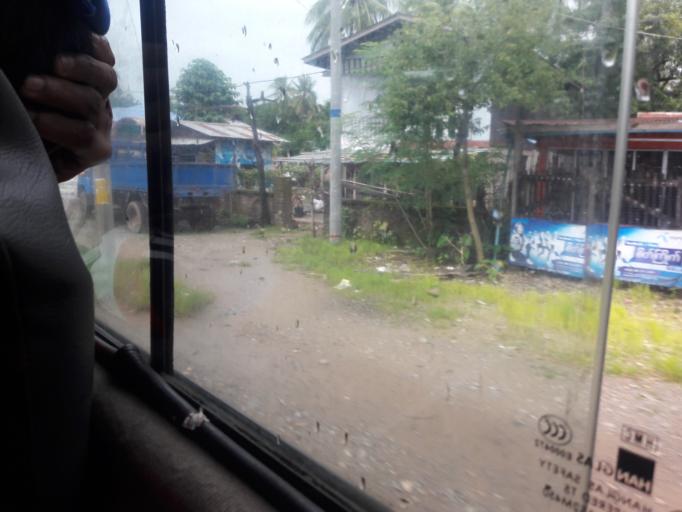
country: MM
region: Bago
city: Nyaunglebin
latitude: 17.7741
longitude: 96.6436
